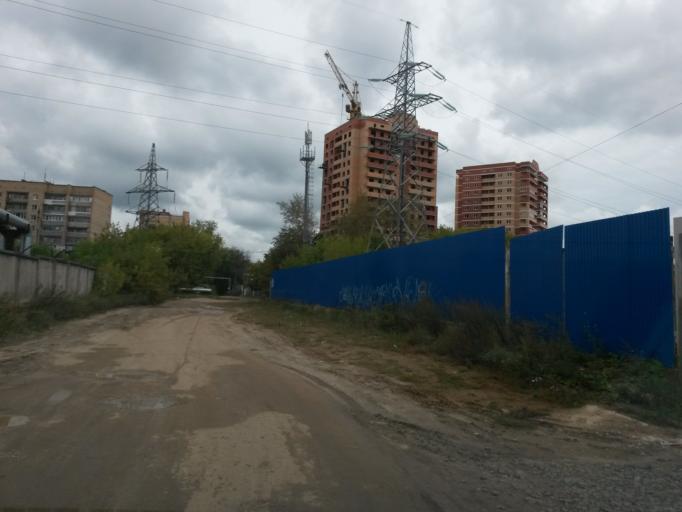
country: RU
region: Moskovskaya
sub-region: Chekhovskiy Rayon
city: Chekhov
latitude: 55.1442
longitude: 37.4780
